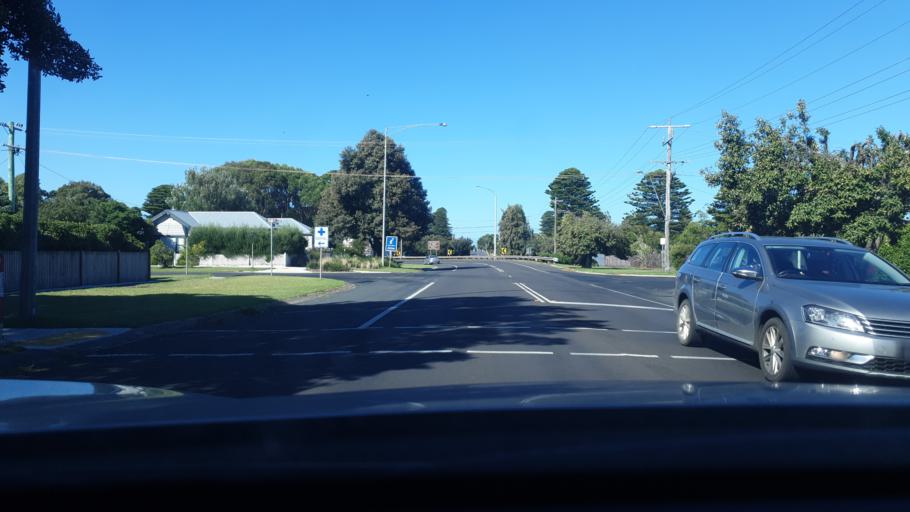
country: AU
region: Victoria
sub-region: Moyne
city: Port Fairy
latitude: -38.3846
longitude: 142.2269
